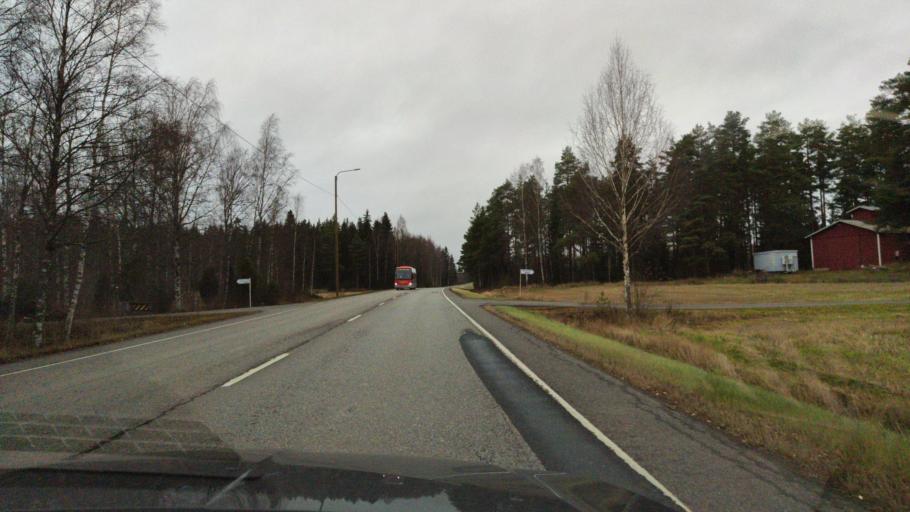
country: FI
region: Satakunta
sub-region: Rauma
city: Kiukainen
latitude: 61.1963
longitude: 22.0561
